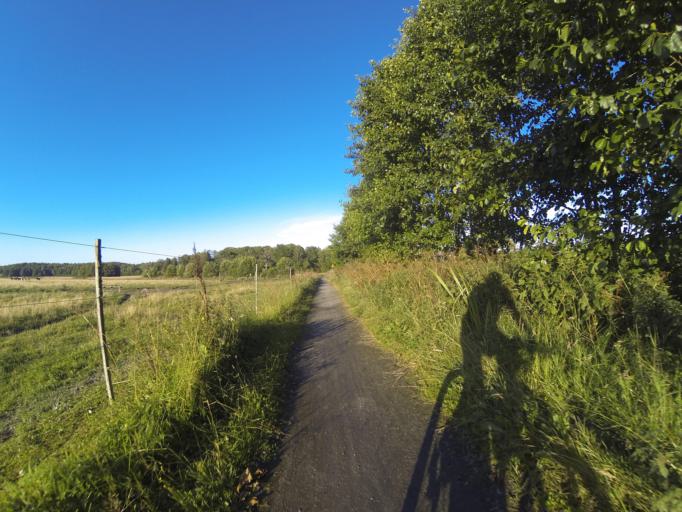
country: SE
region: Vaestmanland
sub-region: Vasteras
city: Vasteras
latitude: 59.5588
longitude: 16.6475
